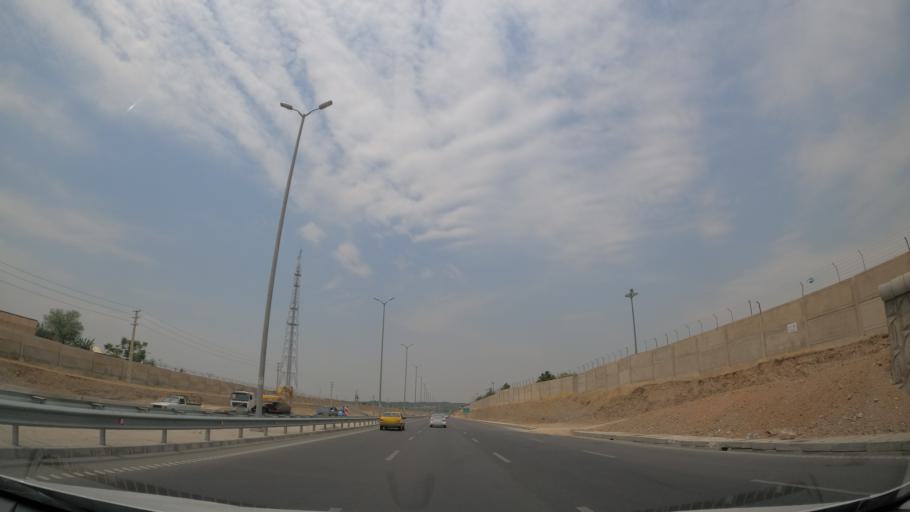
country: IR
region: Tehran
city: Shahr-e Qods
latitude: 35.7409
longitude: 51.2382
